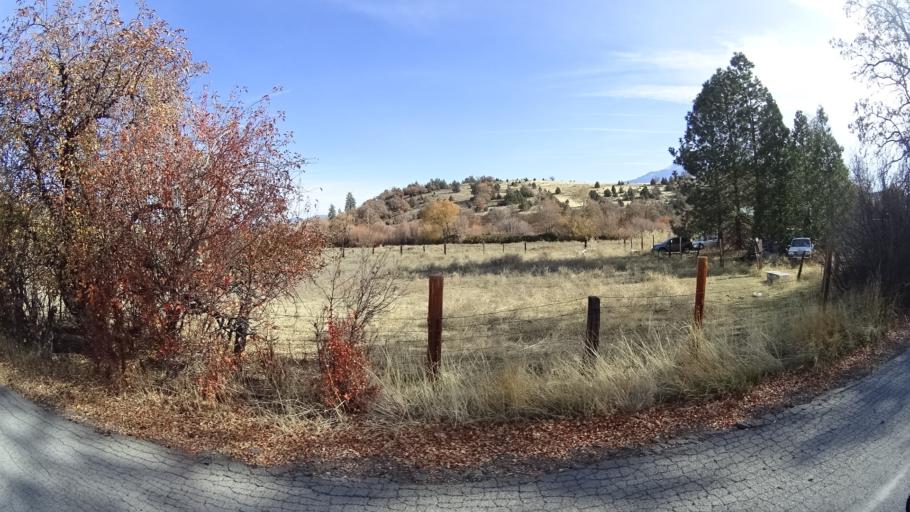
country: US
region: California
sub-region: Siskiyou County
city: Weed
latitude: 41.4785
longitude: -122.4420
